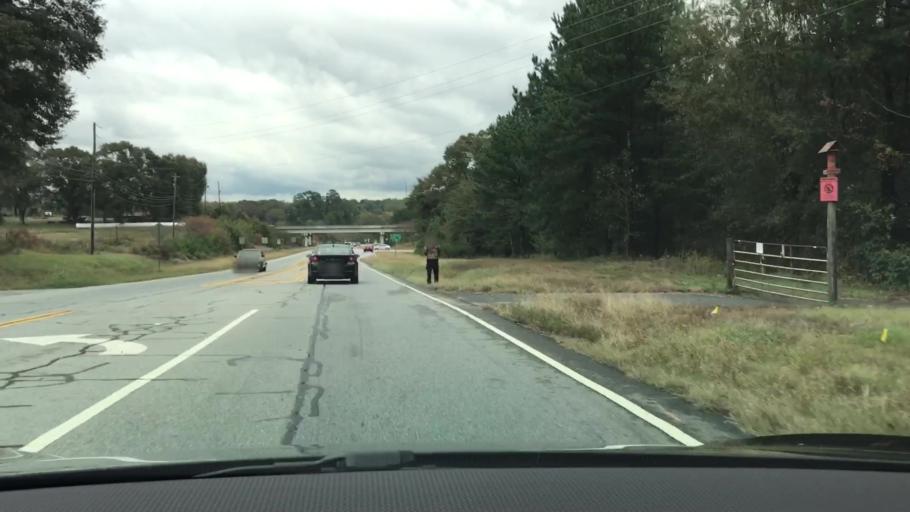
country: US
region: Georgia
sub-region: Oconee County
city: Watkinsville
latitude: 33.8707
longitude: -83.4260
